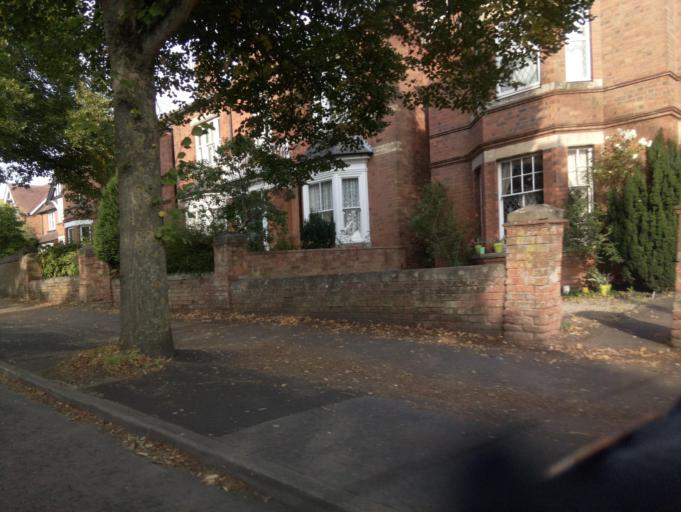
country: GB
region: England
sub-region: Worcestershire
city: Evesham
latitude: 52.0992
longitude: -1.9456
